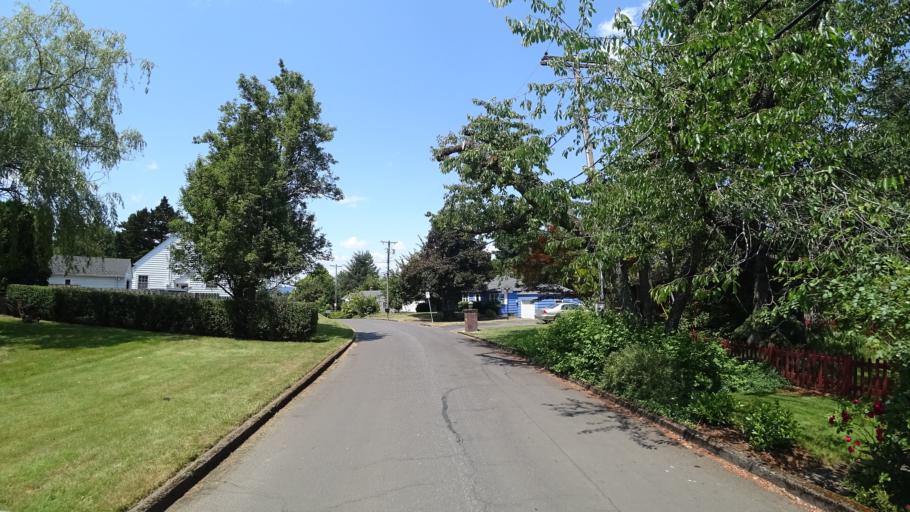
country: US
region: Oregon
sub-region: Multnomah County
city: Lents
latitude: 45.4637
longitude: -122.5654
